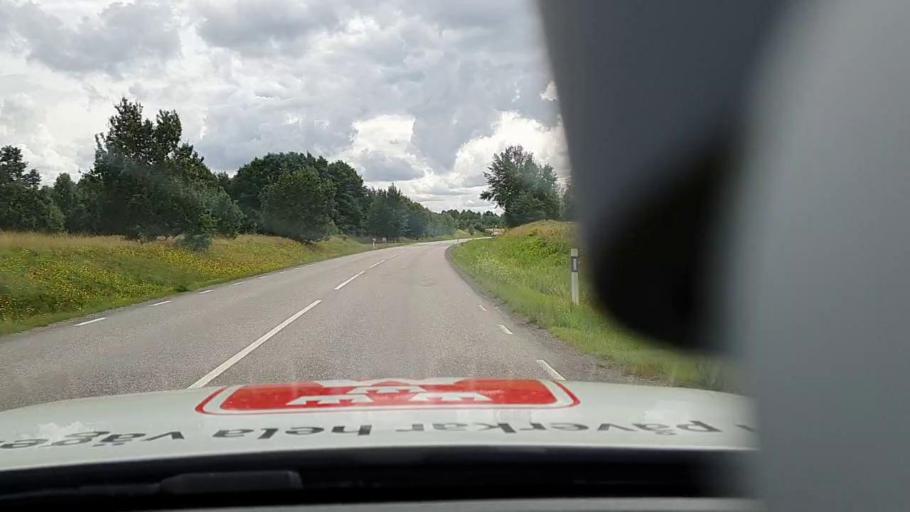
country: SE
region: Vaestra Goetaland
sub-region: Lidkopings Kommun
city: Lidkoping
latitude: 58.5407
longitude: 13.1134
